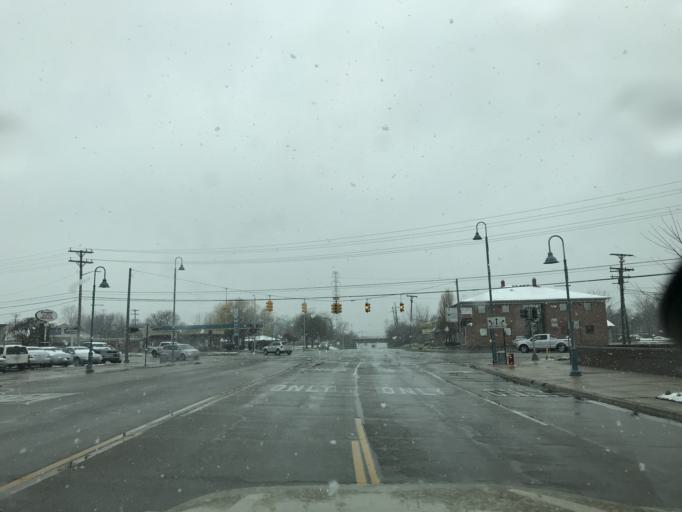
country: US
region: Michigan
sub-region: Wayne County
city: Allen Park
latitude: 42.2569
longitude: -83.2131
